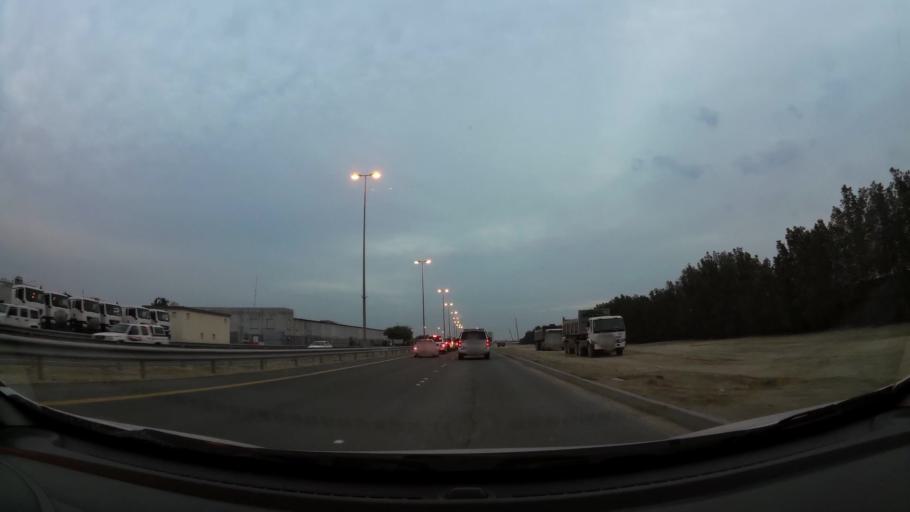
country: BH
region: Northern
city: Ar Rifa'
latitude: 26.1161
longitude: 50.5806
